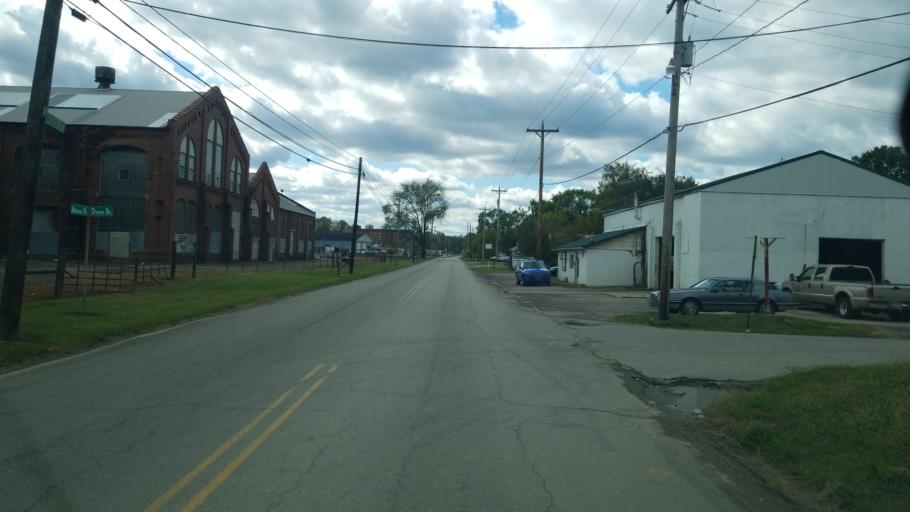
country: US
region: Ohio
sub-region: Jackson County
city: Jackson
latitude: 39.0596
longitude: -82.6309
